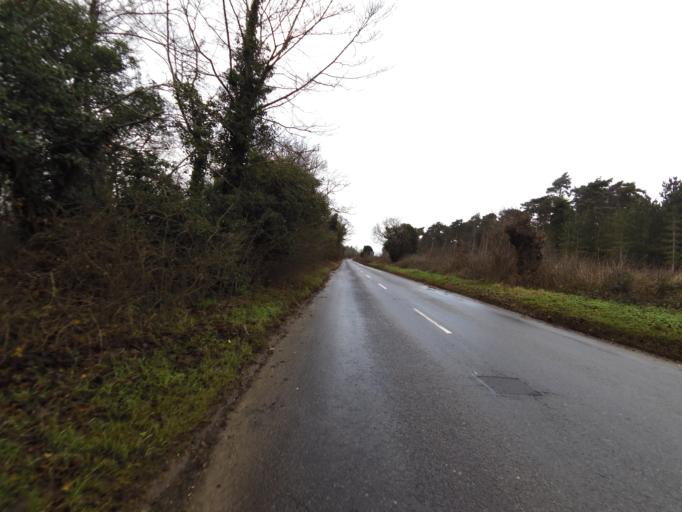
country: GB
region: England
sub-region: Suffolk
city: Needham Market
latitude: 52.1389
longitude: 1.0865
